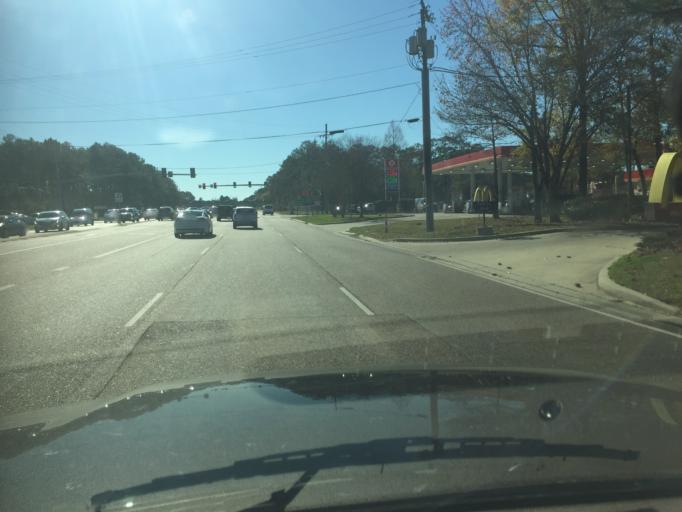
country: US
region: Louisiana
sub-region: Saint Tammany Parish
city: Covington
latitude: 30.4509
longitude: -90.1374
